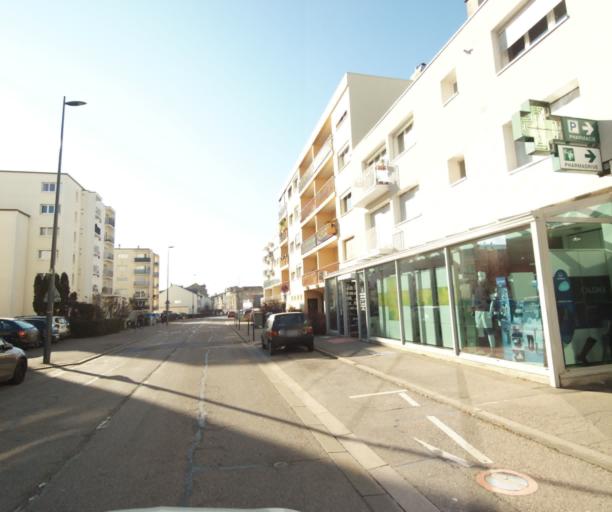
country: FR
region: Lorraine
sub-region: Departement de Meurthe-et-Moselle
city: Saint-Max
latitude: 48.6992
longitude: 6.2104
